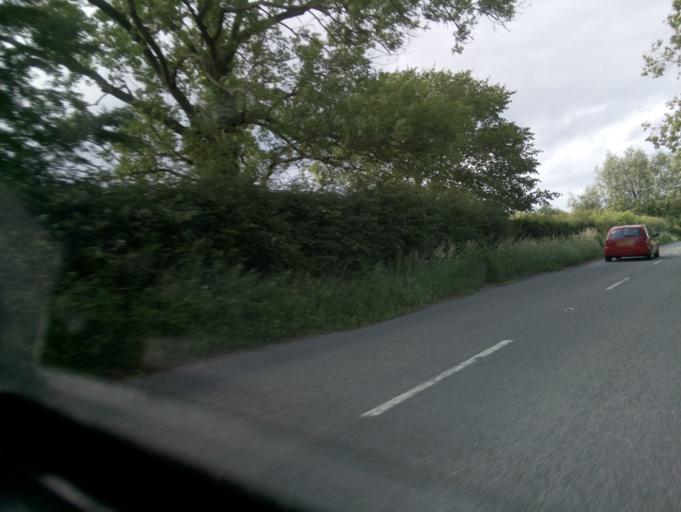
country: GB
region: England
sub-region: Gloucestershire
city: Chipping Campden
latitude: 52.0261
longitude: -1.7400
